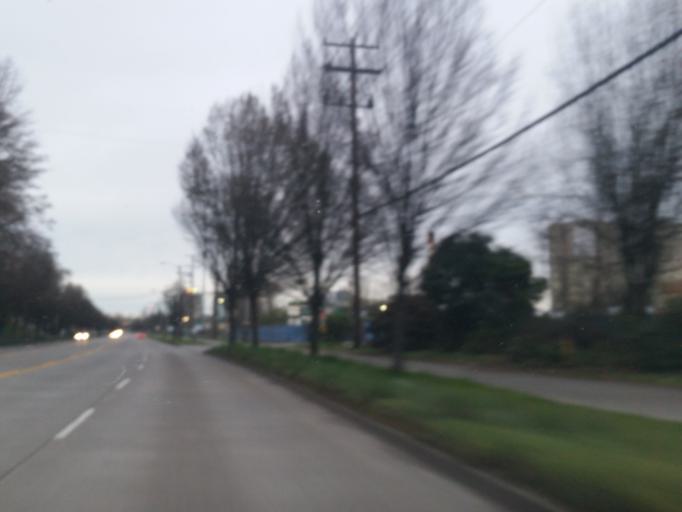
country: US
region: Washington
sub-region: King County
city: White Center
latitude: 47.5475
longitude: -122.3451
